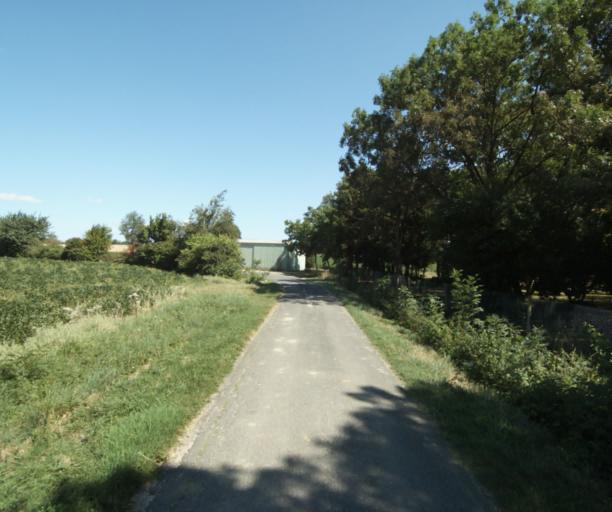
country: FR
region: Midi-Pyrenees
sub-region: Departement de la Haute-Garonne
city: Revel
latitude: 43.4877
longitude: 1.9950
